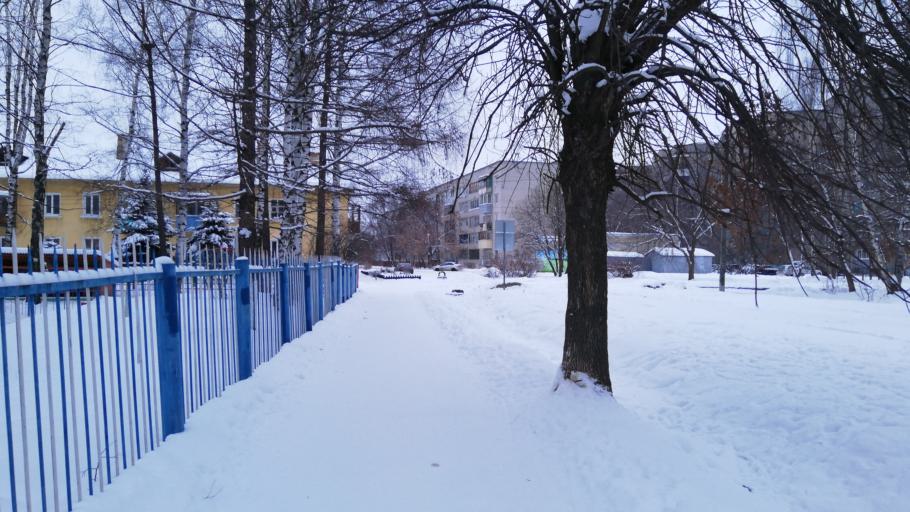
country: RU
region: Jaroslavl
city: Yaroslavl
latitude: 57.5756
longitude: 39.9259
